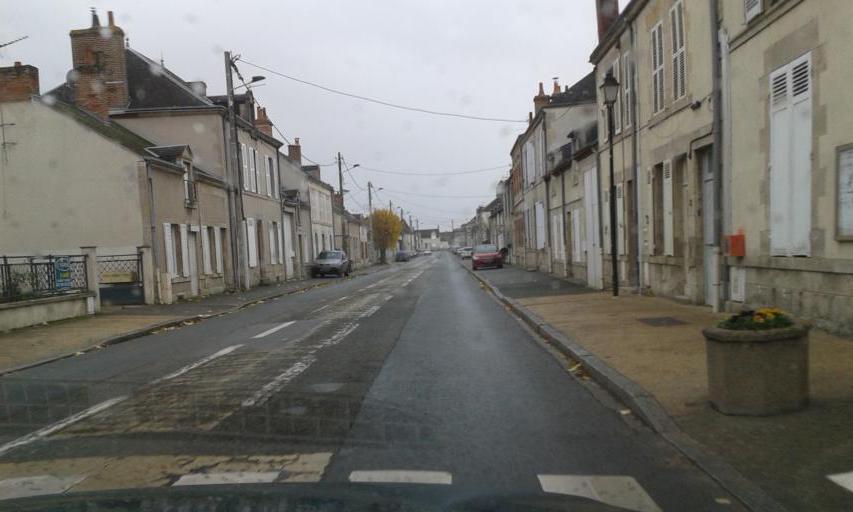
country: FR
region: Centre
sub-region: Departement du Loiret
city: Fay-aux-Loges
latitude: 47.9274
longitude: 2.1382
